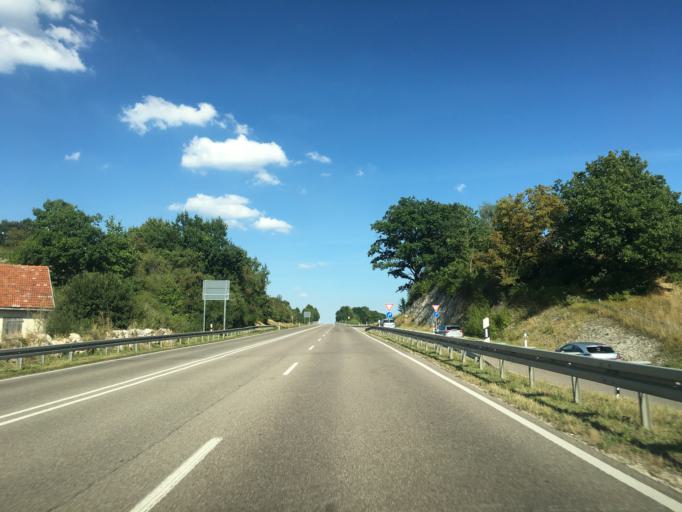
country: DE
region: Baden-Wuerttemberg
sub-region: Tuebingen Region
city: Untermarchtal
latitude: 48.2460
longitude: 9.6136
